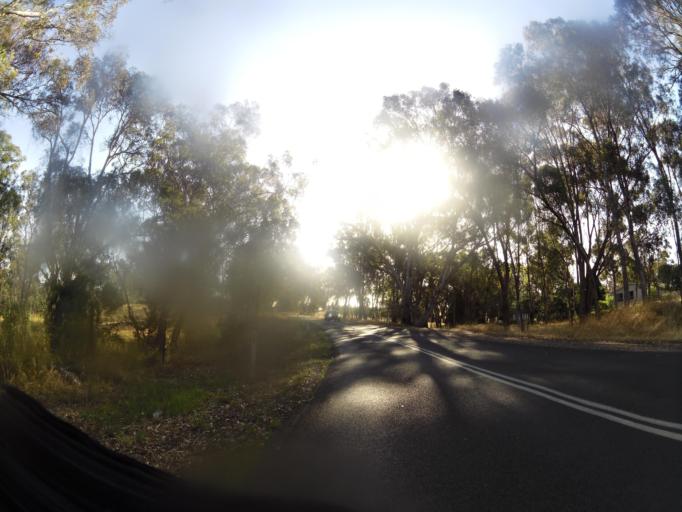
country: AU
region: Victoria
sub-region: Murrindindi
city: Kinglake West
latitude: -37.0202
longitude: 145.1074
